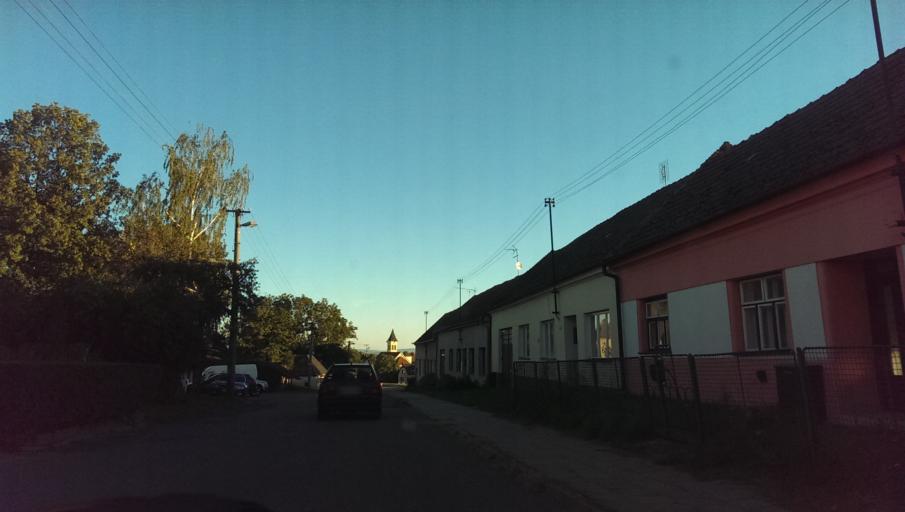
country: CZ
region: Zlin
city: Zlechov
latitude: 49.0761
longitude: 17.3783
